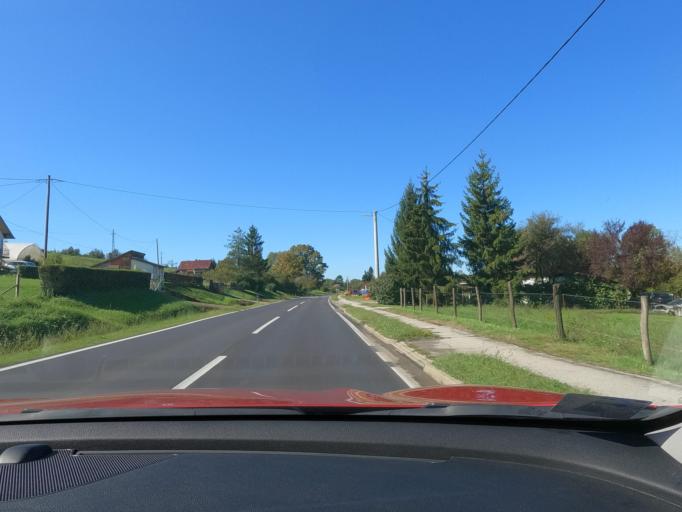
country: HR
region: Sisacko-Moslavacka
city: Osekovo
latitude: 45.5303
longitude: 16.5526
